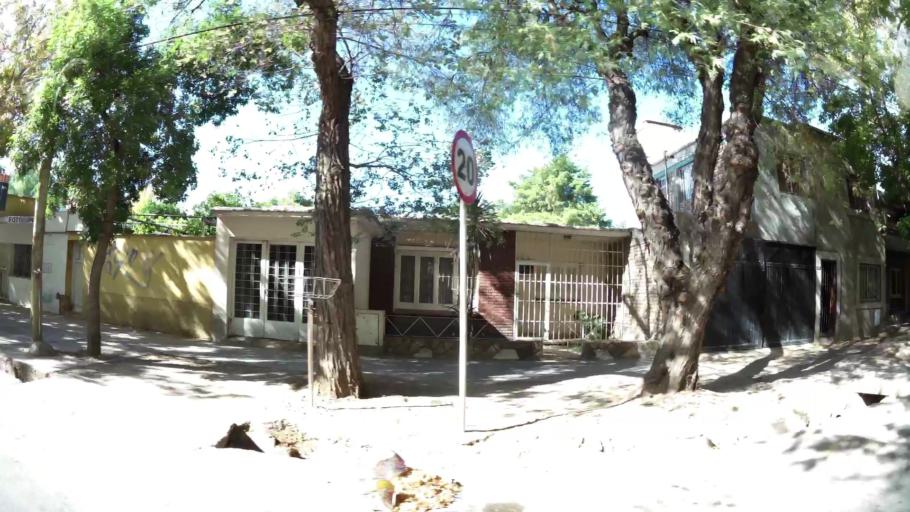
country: AR
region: Mendoza
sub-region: Departamento de Godoy Cruz
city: Godoy Cruz
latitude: -32.9251
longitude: -68.8526
